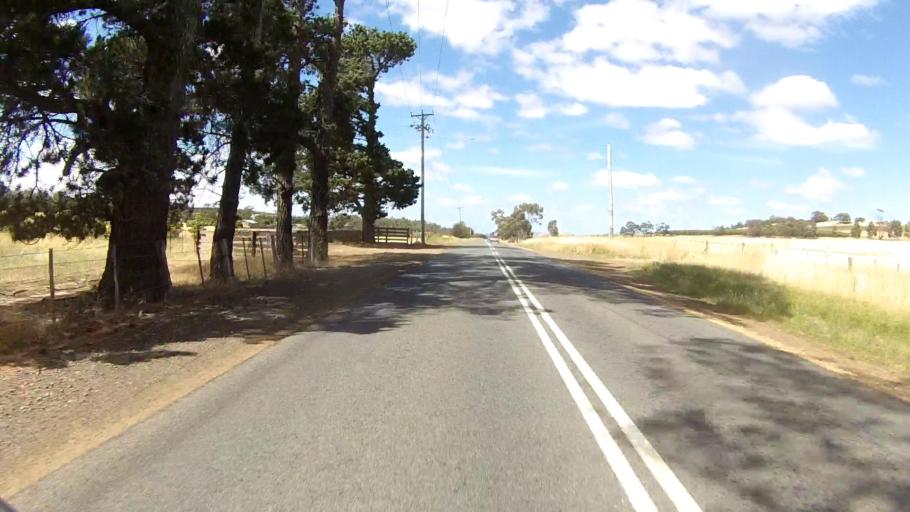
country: AU
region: Tasmania
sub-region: Sorell
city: Sorell
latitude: -42.6404
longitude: 147.4334
